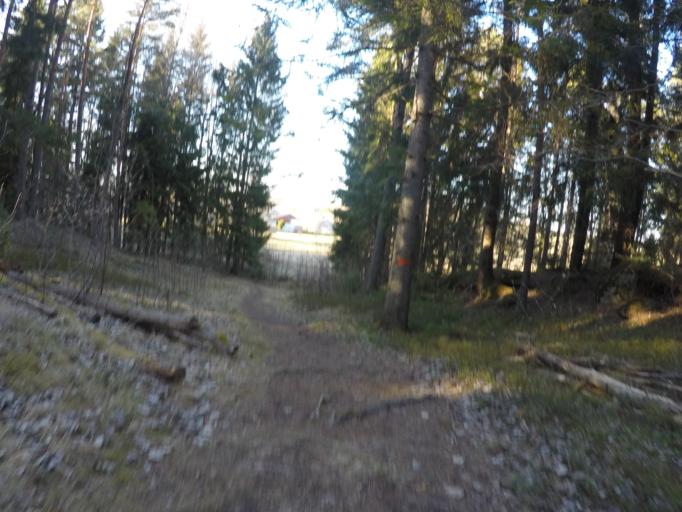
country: SE
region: Soedermanland
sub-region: Eskilstuna Kommun
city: Torshalla
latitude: 59.4102
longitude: 16.4941
